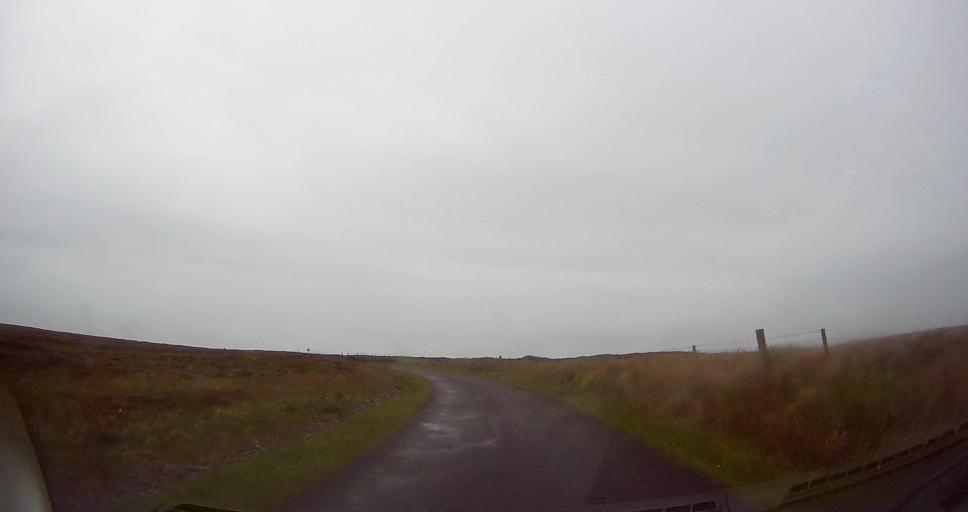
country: GB
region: Scotland
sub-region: Orkney Islands
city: Orkney
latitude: 59.1045
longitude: -3.1329
